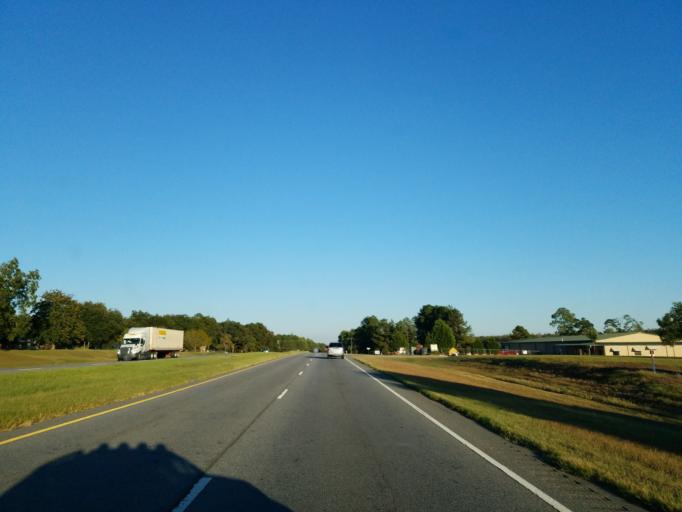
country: US
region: Georgia
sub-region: Worth County
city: Sylvester
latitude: 31.5091
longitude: -83.7439
